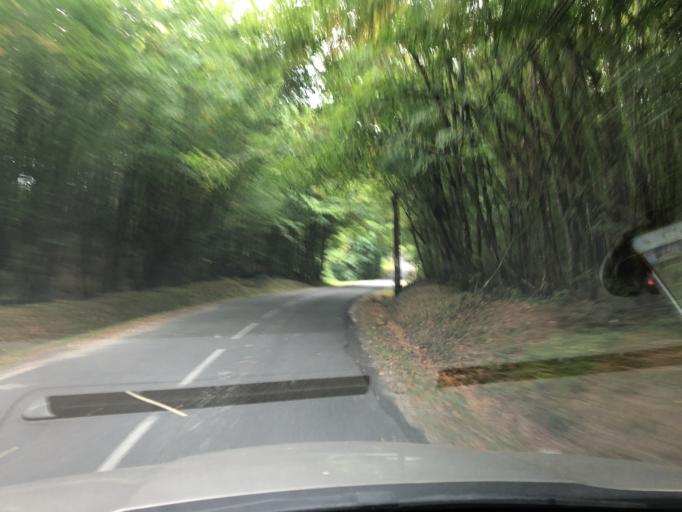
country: FR
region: Centre
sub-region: Departement d'Indre-et-Loire
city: Mazieres-de-Touraine
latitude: 47.3901
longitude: 0.4483
